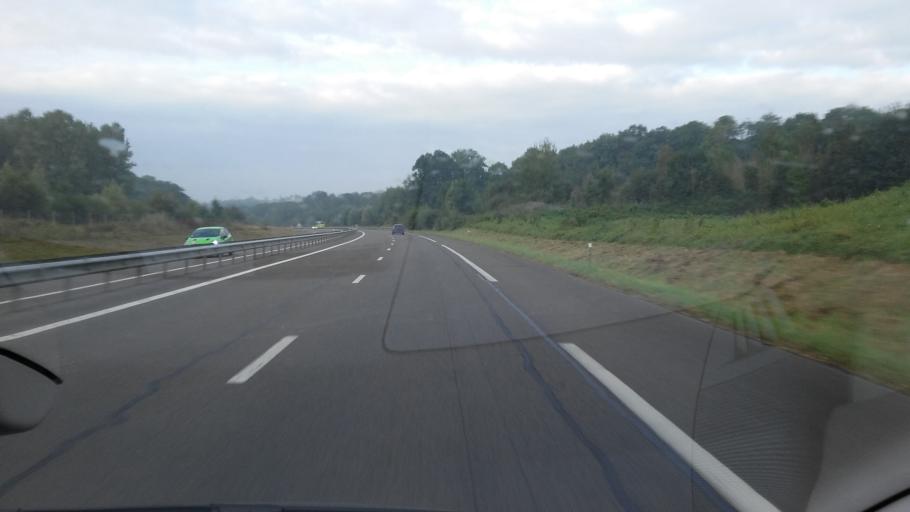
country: FR
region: Champagne-Ardenne
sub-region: Departement des Ardennes
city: Prix-les-Mezieres
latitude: 49.6440
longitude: 4.5786
